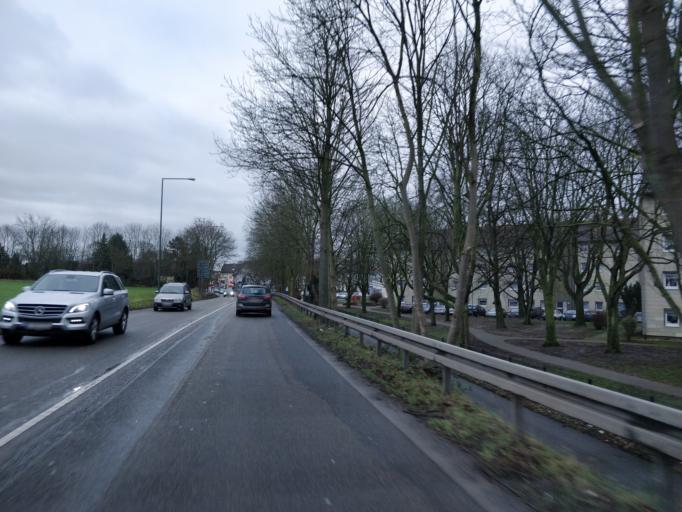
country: DE
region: North Rhine-Westphalia
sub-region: Regierungsbezirk Koln
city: Eil
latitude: 50.8847
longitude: 7.0813
